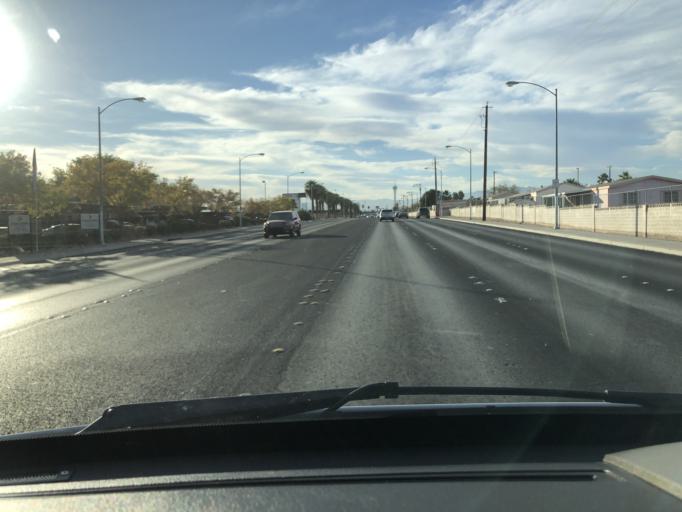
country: US
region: Nevada
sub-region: Clark County
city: Winchester
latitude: 36.1463
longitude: -115.0951
